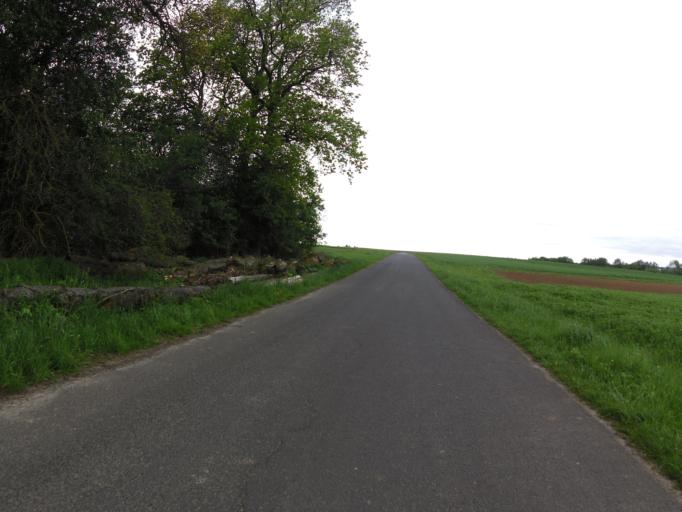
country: DE
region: Bavaria
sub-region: Regierungsbezirk Unterfranken
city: Unterpleichfeld
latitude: 49.8446
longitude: 10.0655
